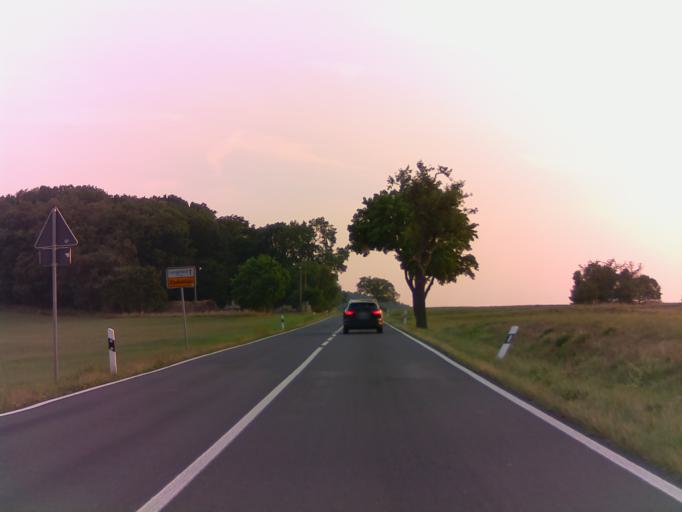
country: DE
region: Thuringia
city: Blankenhain
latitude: 50.8528
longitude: 11.3408
